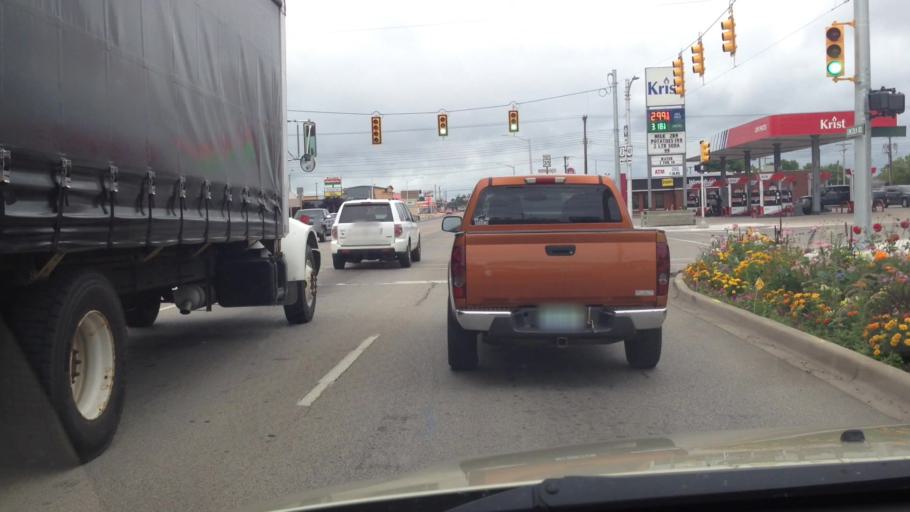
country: US
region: Michigan
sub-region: Delta County
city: Escanaba
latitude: 45.7454
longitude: -87.0798
